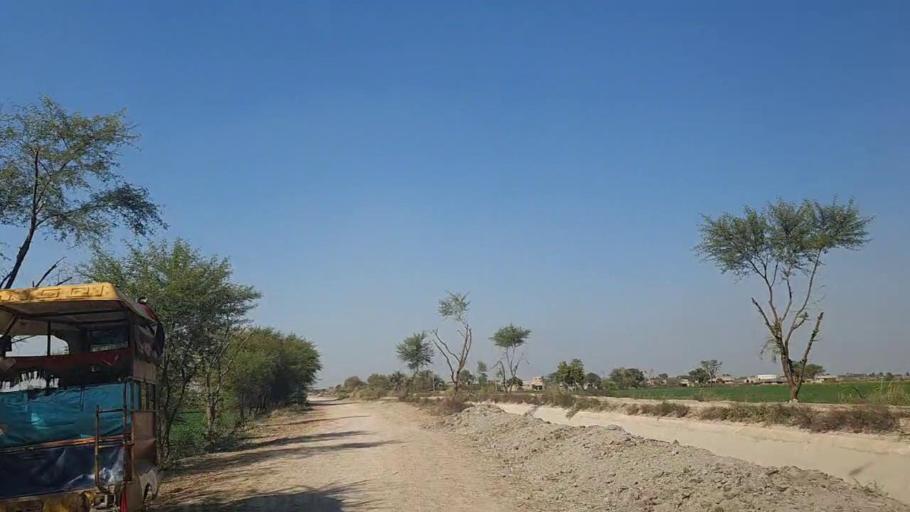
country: PK
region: Sindh
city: Sakrand
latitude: 26.2724
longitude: 68.2204
